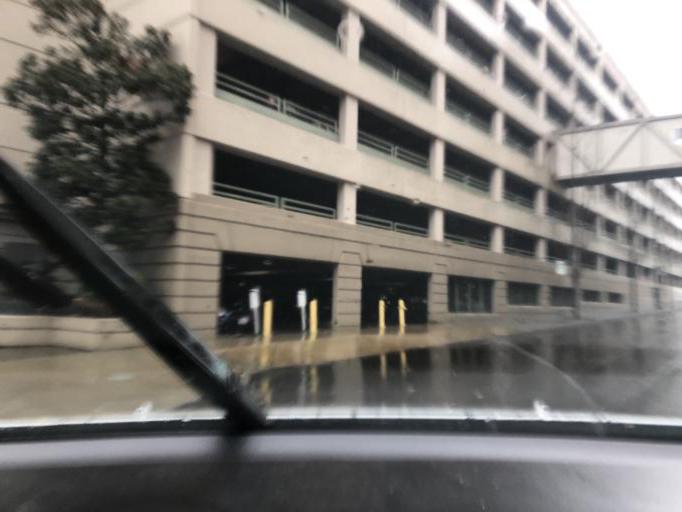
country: US
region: Washington
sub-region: Pierce County
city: Tacoma
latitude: 47.2536
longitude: -122.4372
